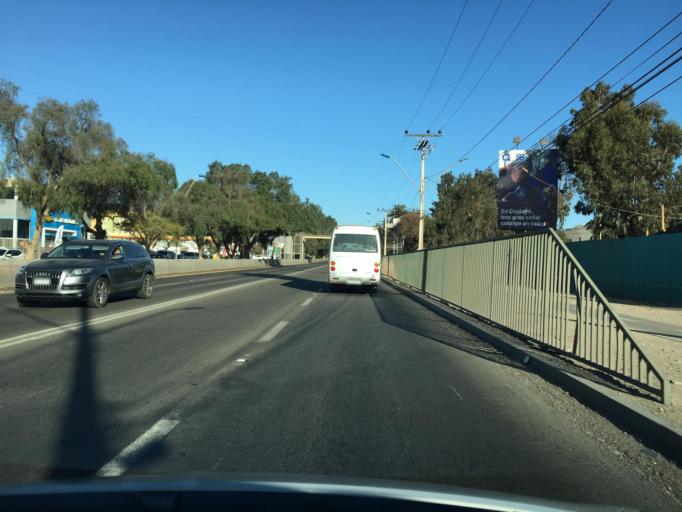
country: CL
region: Atacama
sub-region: Provincia de Copiapo
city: Copiapo
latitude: -27.3603
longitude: -70.3501
